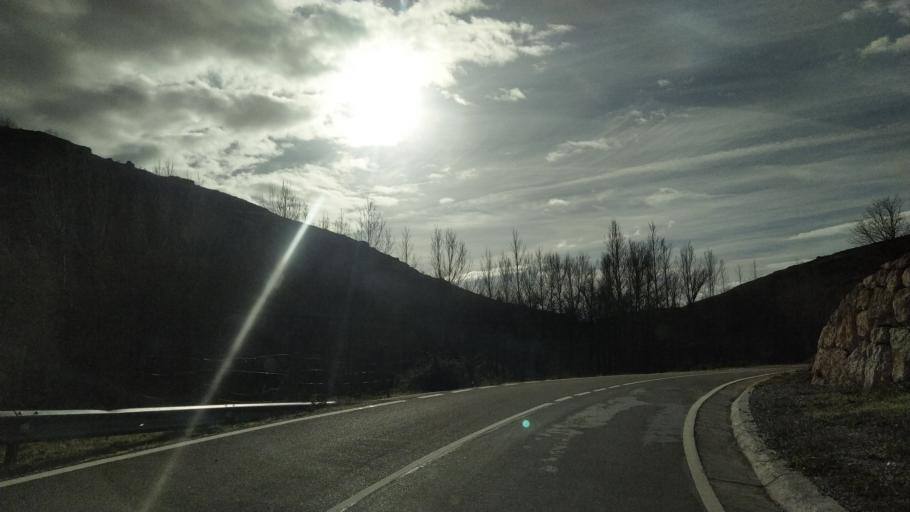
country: ES
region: Cantabria
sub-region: Provincia de Cantabria
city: San Martin de Elines
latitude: 42.8507
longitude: -3.9102
